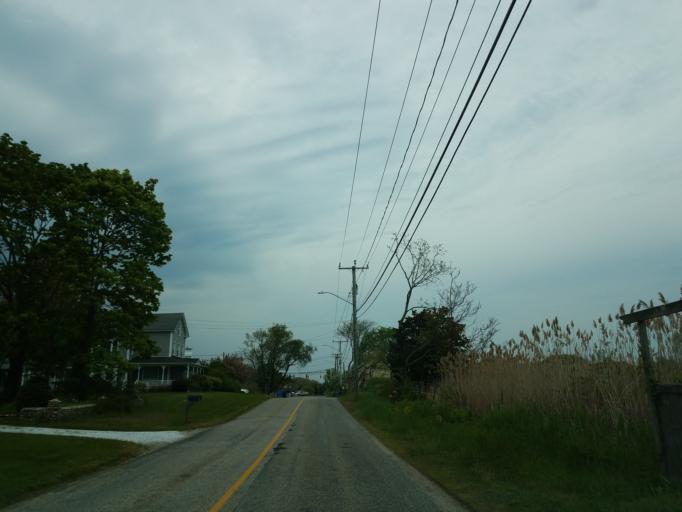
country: US
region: Connecticut
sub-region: Middlesex County
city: Saybrook Manor
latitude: 41.2863
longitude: -72.3942
